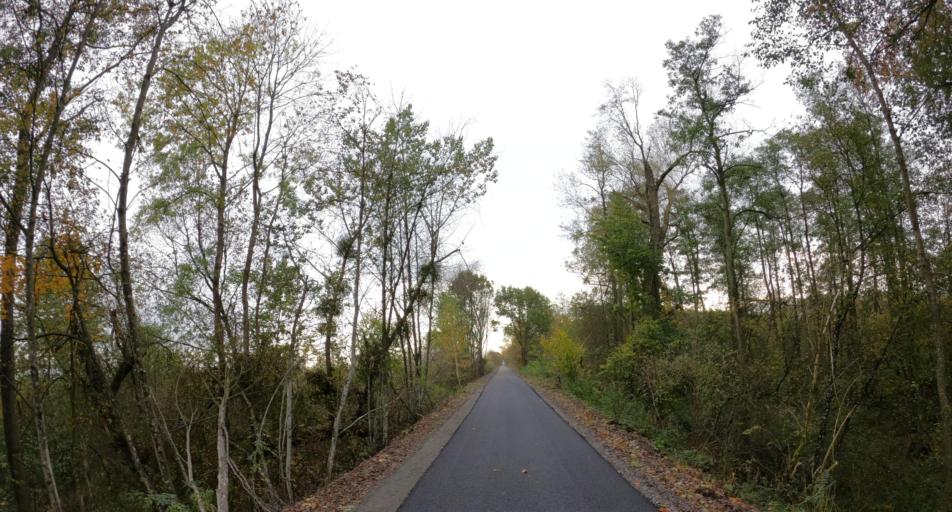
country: PL
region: West Pomeranian Voivodeship
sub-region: Powiat mysliborski
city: Nowogrodek Pomorski
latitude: 52.9867
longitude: 15.0894
